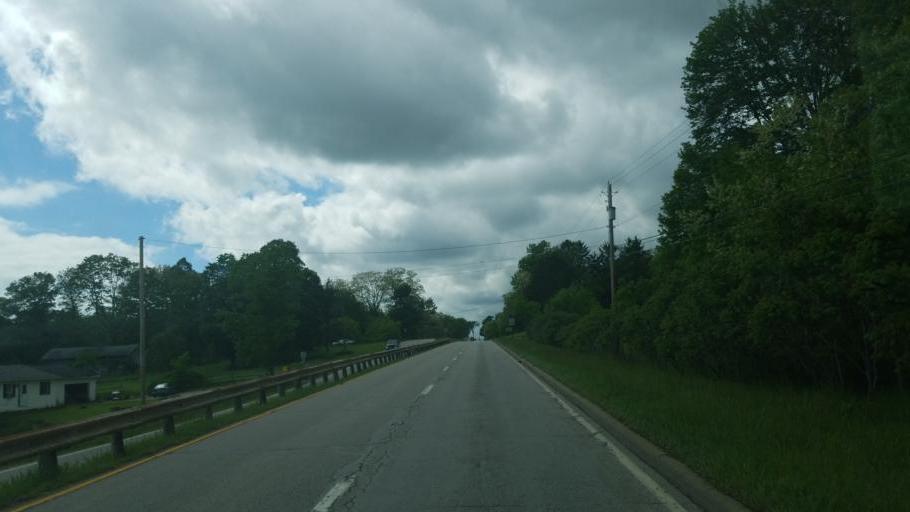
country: US
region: Ohio
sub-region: Portage County
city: Hiram
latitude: 41.3718
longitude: -81.0890
